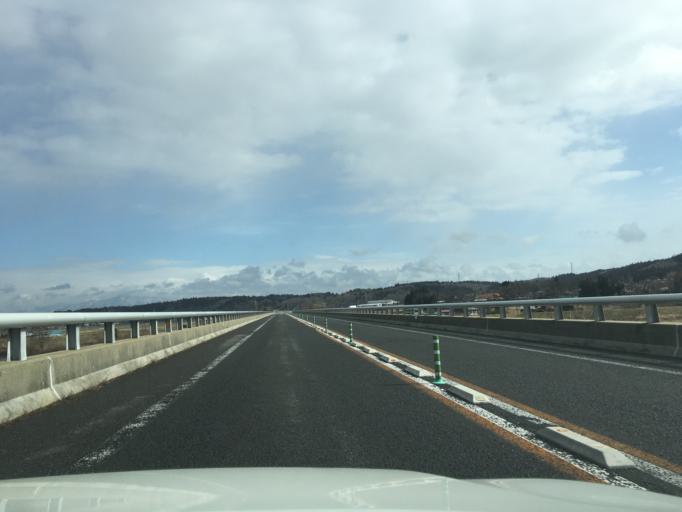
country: JP
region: Akita
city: Akita
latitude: 39.6202
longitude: 140.1502
